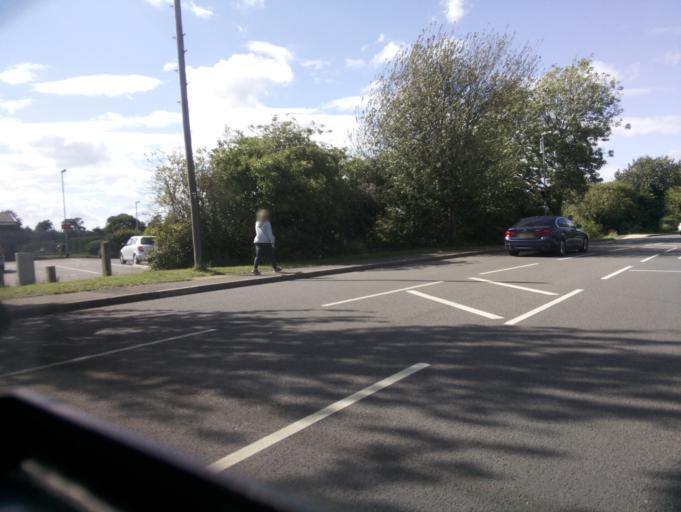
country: GB
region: England
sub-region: Nottinghamshire
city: East Leake
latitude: 52.8325
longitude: -1.1775
